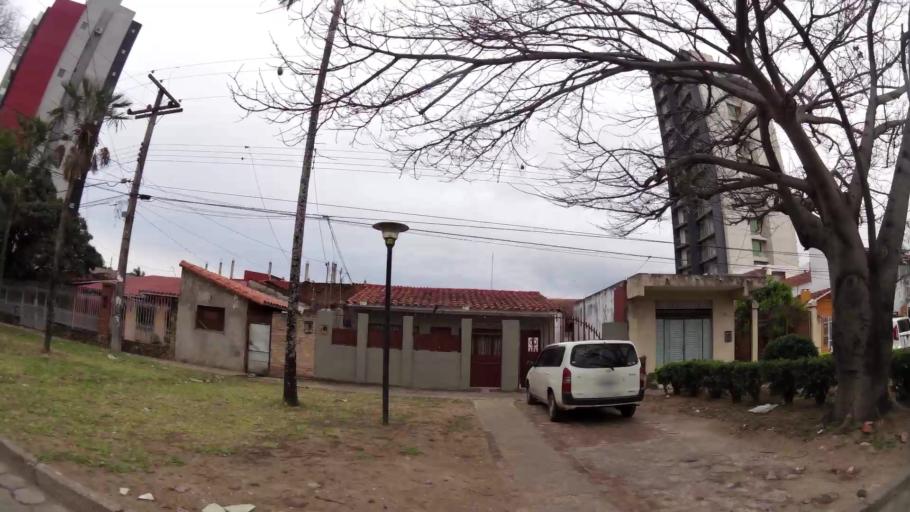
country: BO
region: Santa Cruz
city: Santa Cruz de la Sierra
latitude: -17.7991
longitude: -63.1907
